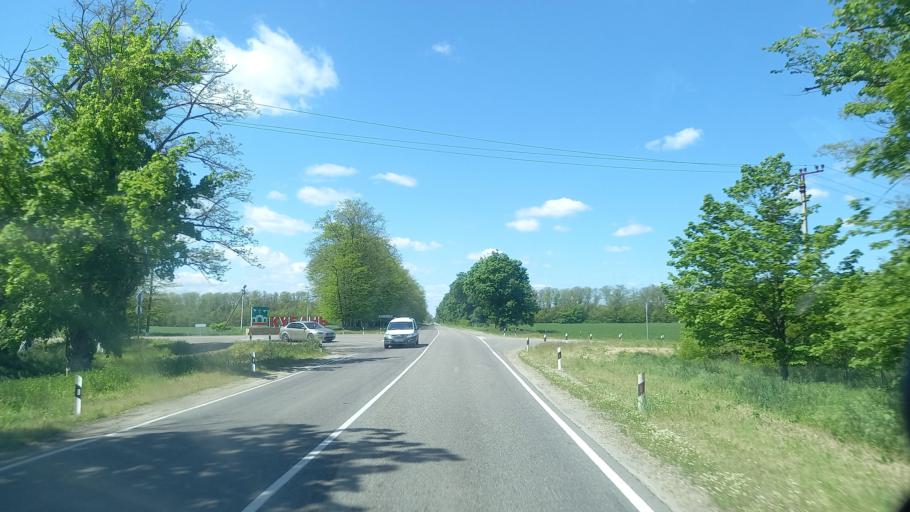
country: RU
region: Krasnodarskiy
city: Kazanskaya
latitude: 45.3687
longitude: 40.4239
